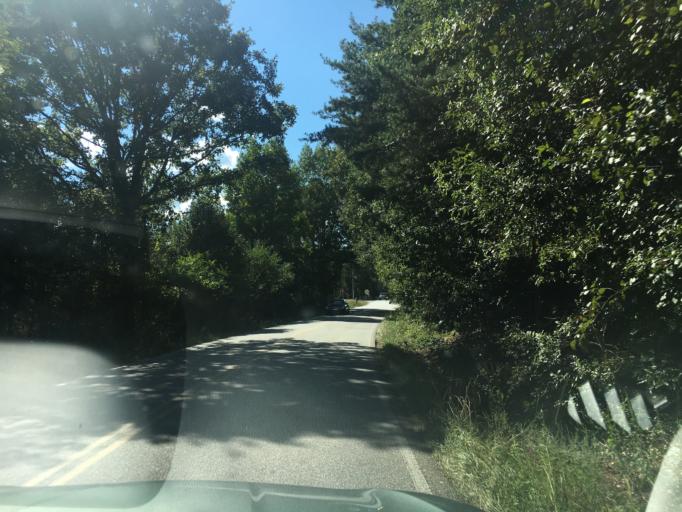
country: US
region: South Carolina
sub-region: Greenville County
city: Five Forks
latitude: 34.8222
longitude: -82.2270
